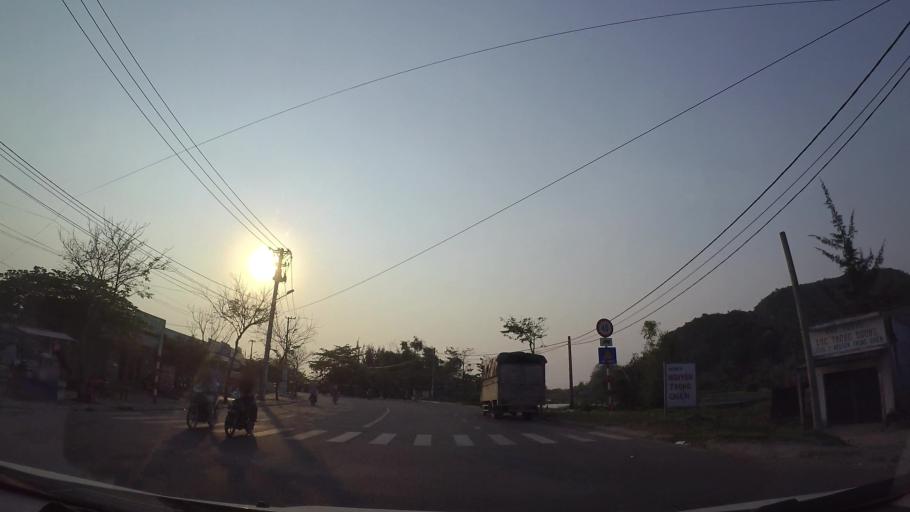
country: VN
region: Da Nang
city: Ngu Hanh Son
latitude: 15.9958
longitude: 108.2581
